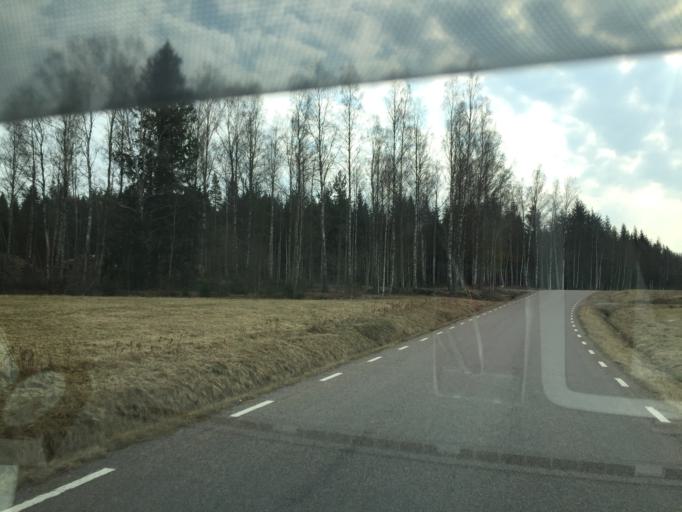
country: SE
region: Soedermanland
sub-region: Vingakers Kommun
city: Vingaker
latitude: 58.9995
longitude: 15.6761
